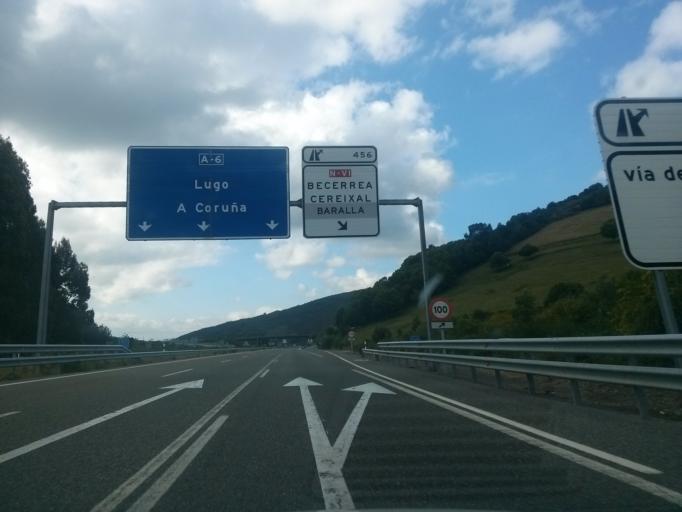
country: ES
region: Galicia
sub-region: Provincia de Lugo
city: Becerrea
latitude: 42.8756
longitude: -7.1758
